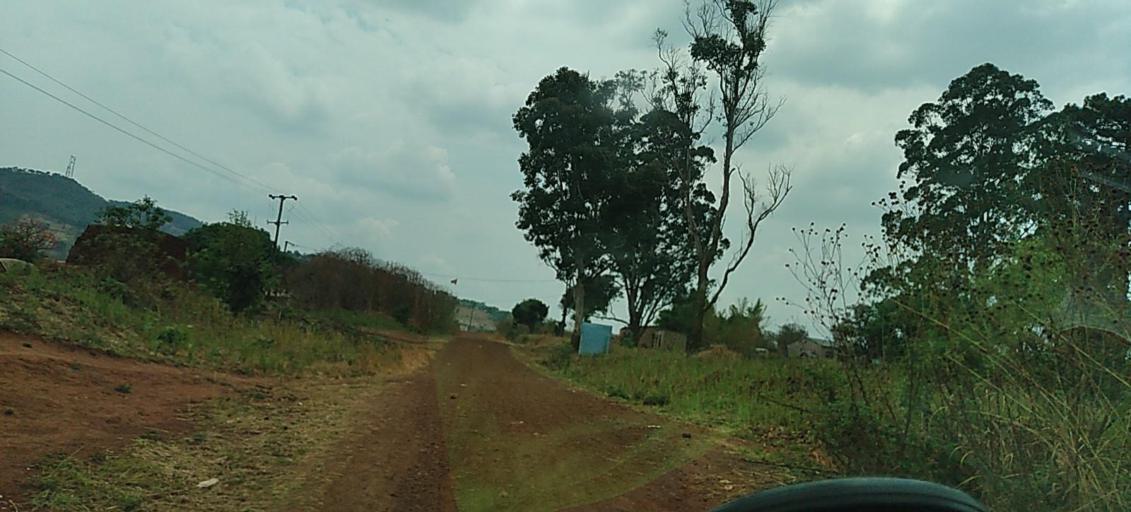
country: ZM
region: North-Western
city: Kansanshi
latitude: -12.0315
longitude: 26.4354
